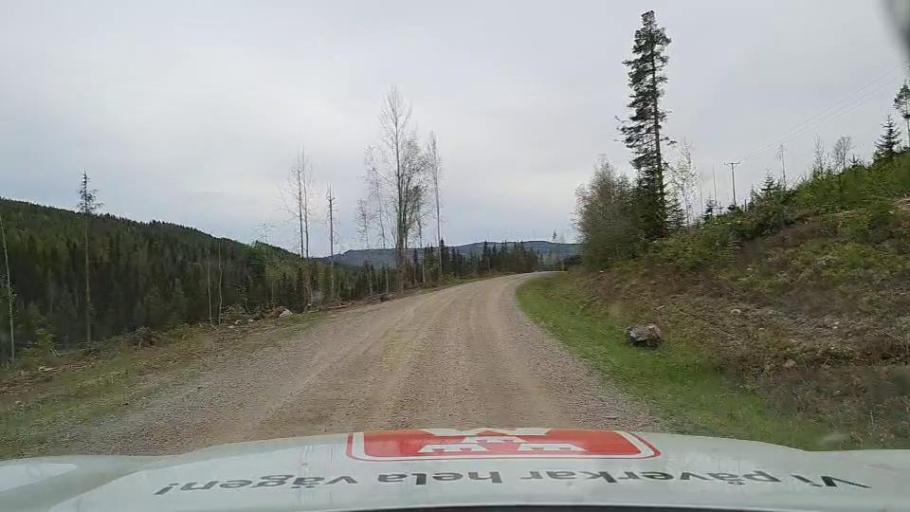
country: SE
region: Jaemtland
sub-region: Bergs Kommun
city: Hoverberg
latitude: 62.5276
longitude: 14.7115
